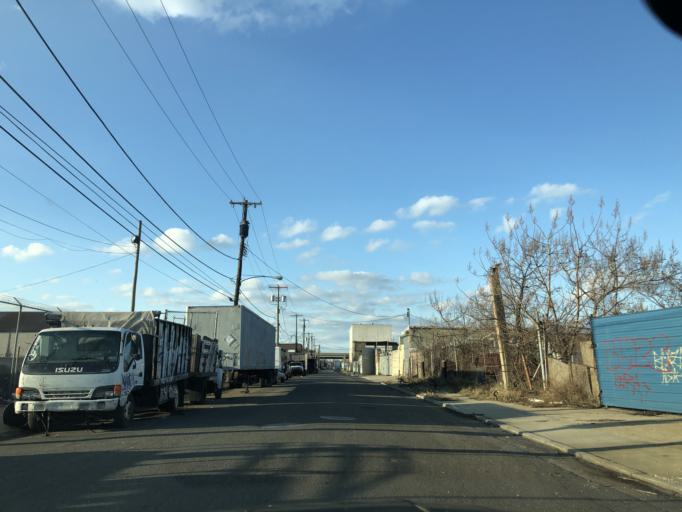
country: US
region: New Jersey
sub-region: Camden County
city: Merchantville
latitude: 39.9815
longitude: -75.0931
